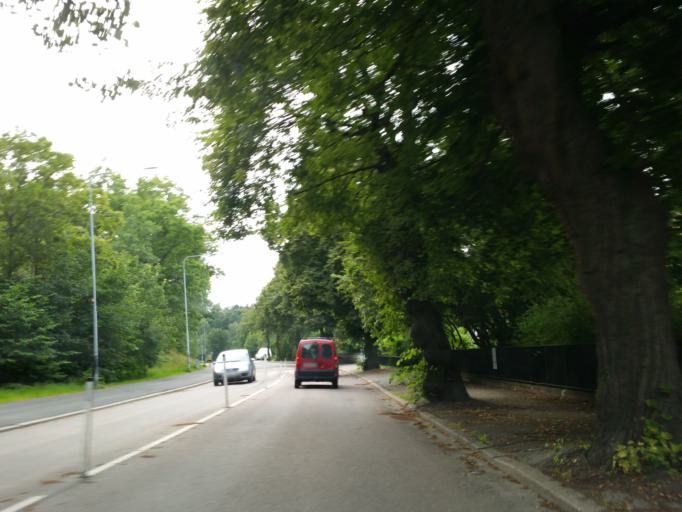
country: SE
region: Stockholm
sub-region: Solna Kommun
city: Rasunda
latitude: 59.3704
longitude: 17.9868
